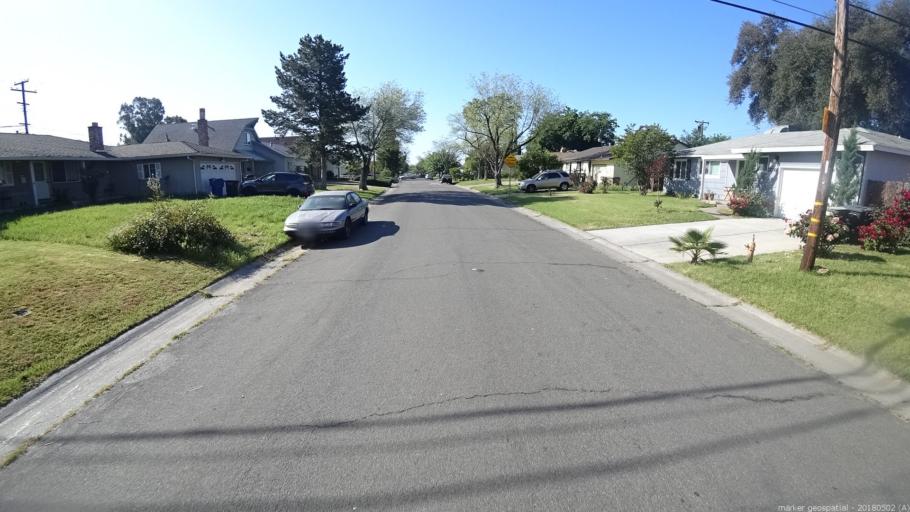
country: US
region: California
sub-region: Sacramento County
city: Arden-Arcade
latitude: 38.6065
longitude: -121.4241
